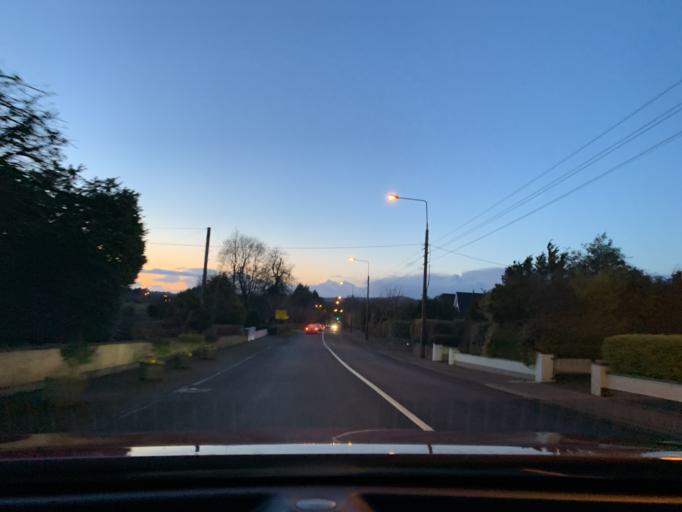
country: IE
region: Connaught
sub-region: Roscommon
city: Boyle
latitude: 53.9712
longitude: -8.2880
